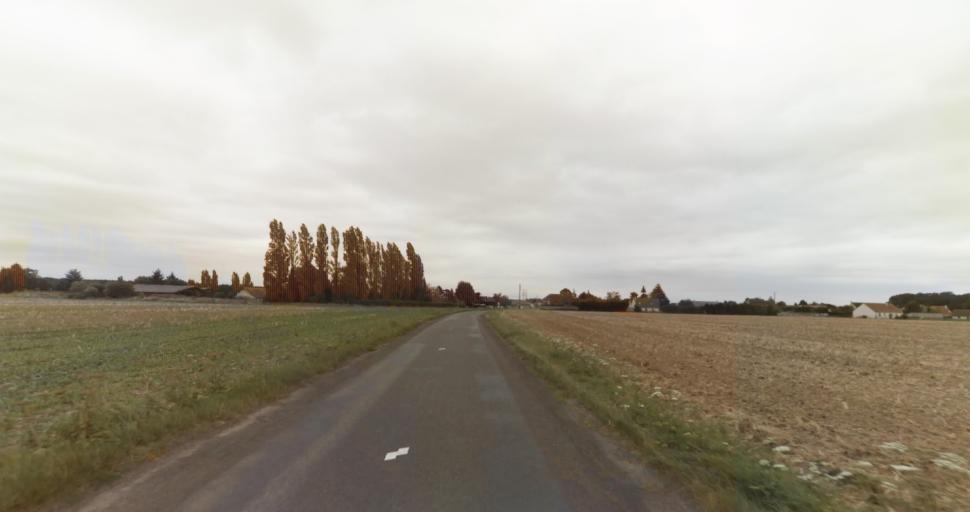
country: FR
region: Haute-Normandie
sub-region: Departement de l'Eure
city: La Couture-Boussey
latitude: 48.9157
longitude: 1.4058
